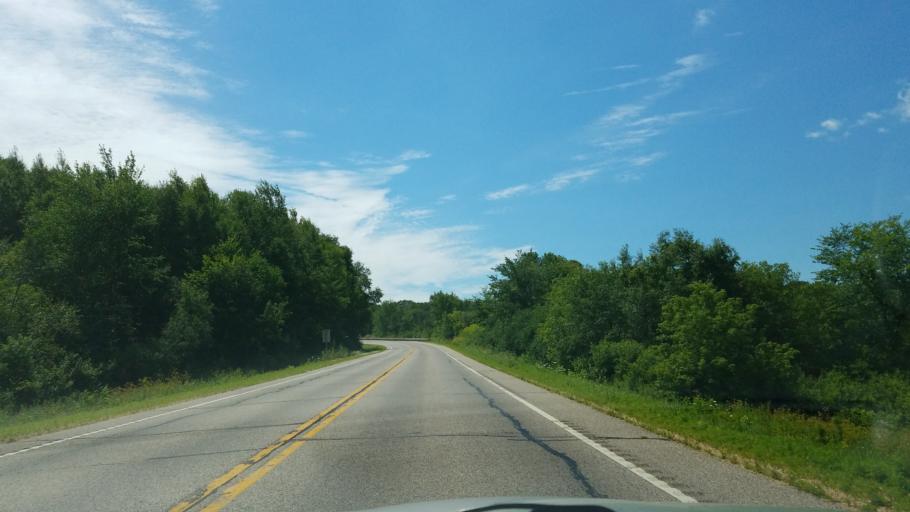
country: US
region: Wisconsin
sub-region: Saint Croix County
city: Glenwood City
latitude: 45.0312
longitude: -92.1918
